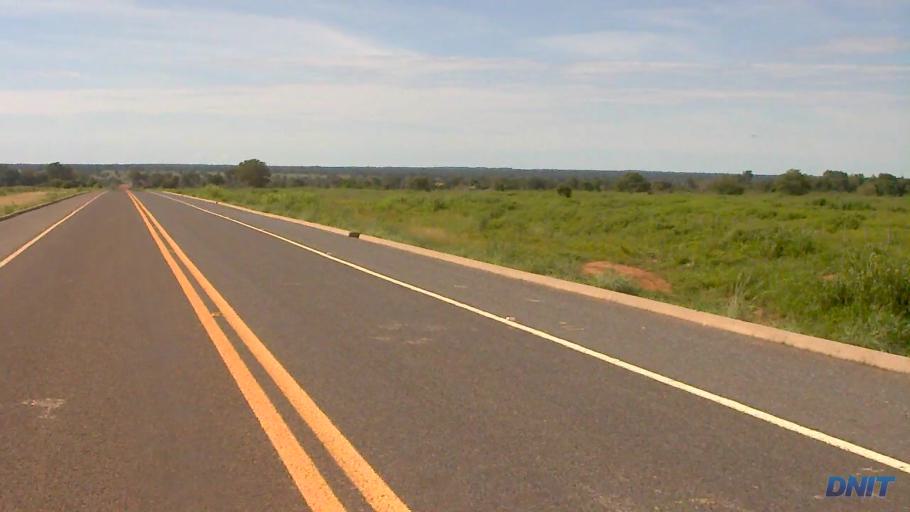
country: BR
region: Goias
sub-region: Sao Miguel Do Araguaia
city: Sao Miguel do Araguaia
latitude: -13.4857
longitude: -50.1105
